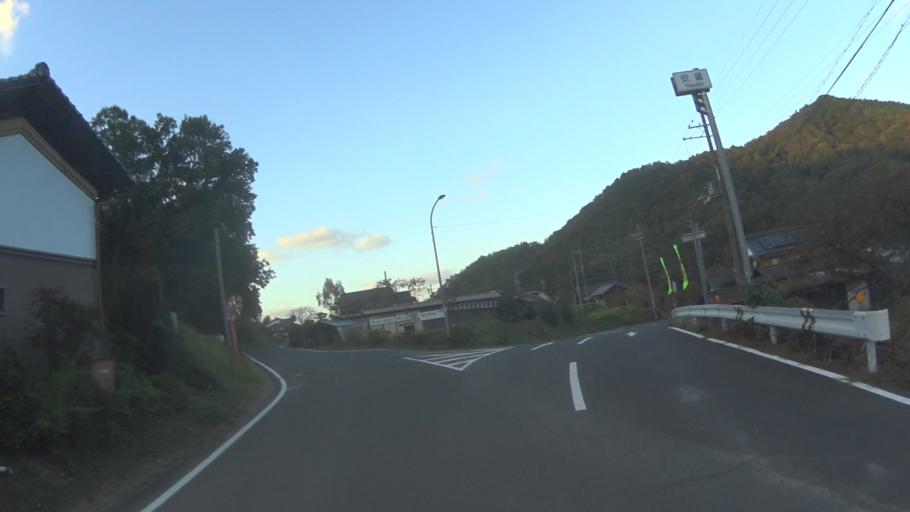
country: JP
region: Kyoto
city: Ayabe
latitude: 35.2890
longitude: 135.2380
